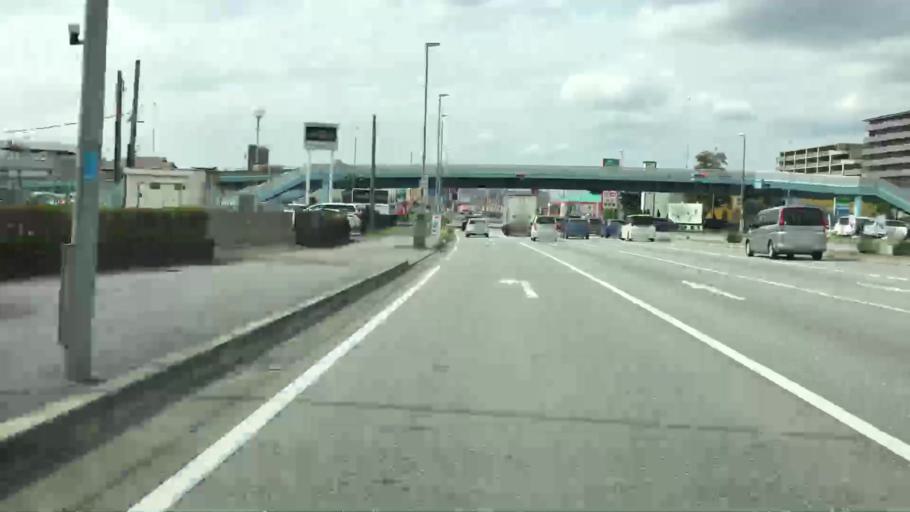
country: JP
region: Tochigi
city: Sano
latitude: 36.2961
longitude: 139.6054
